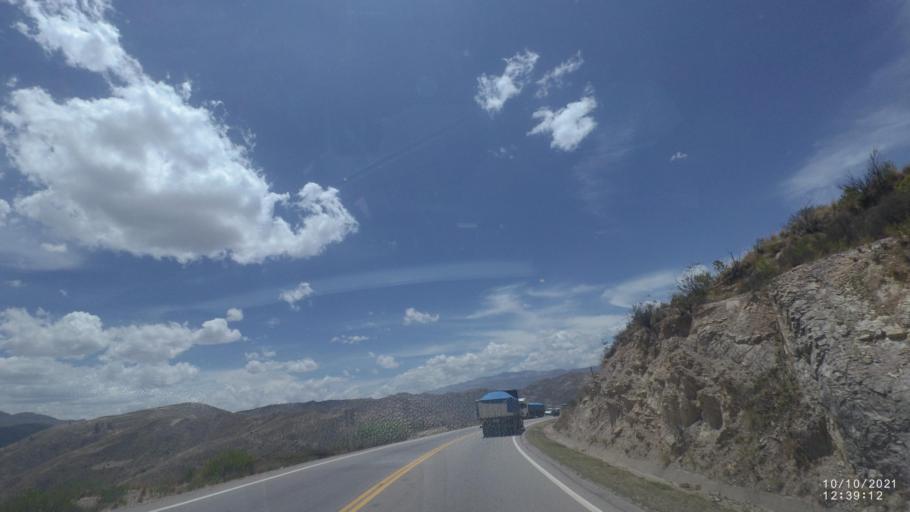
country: BO
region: Cochabamba
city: Irpa Irpa
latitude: -17.6467
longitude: -66.3930
